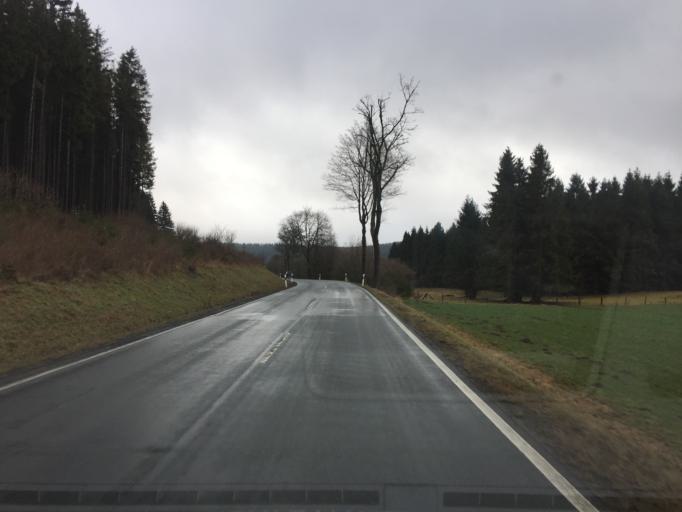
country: DE
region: North Rhine-Westphalia
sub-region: Regierungsbezirk Arnsberg
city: Winterberg
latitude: 51.2212
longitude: 8.5847
